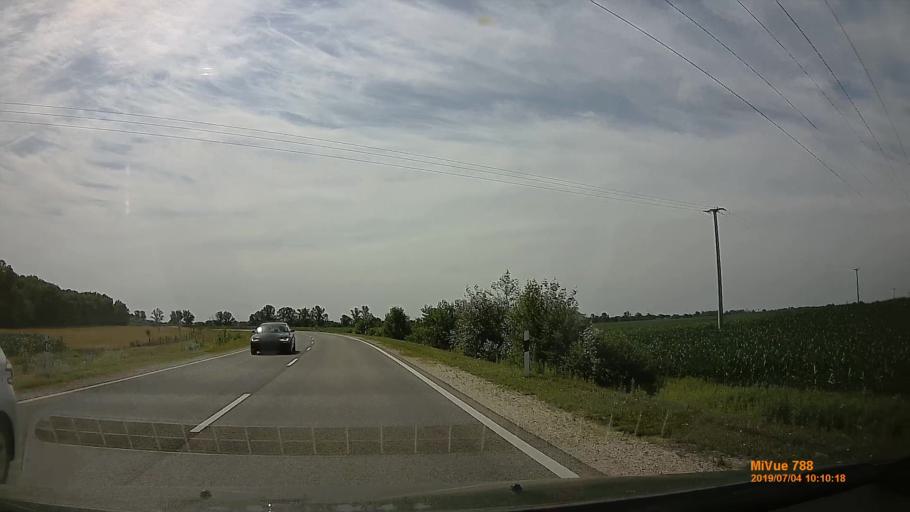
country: HU
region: Komarom-Esztergom
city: Komarom
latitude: 47.7214
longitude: 18.1099
